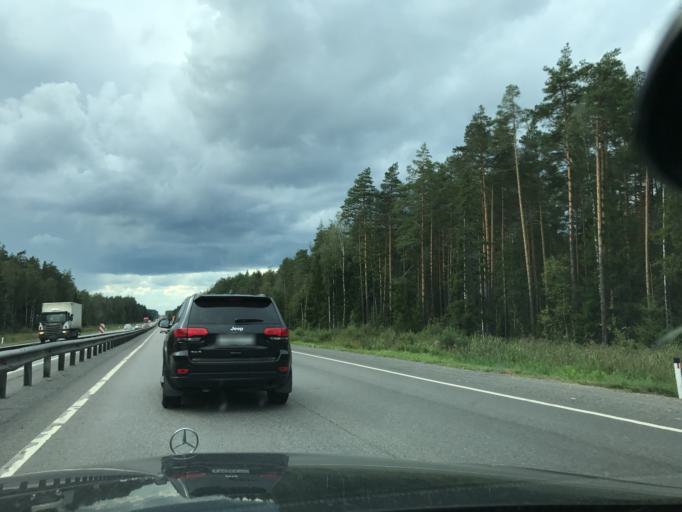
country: RU
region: Vladimir
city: Petushki
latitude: 55.9298
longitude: 39.3460
